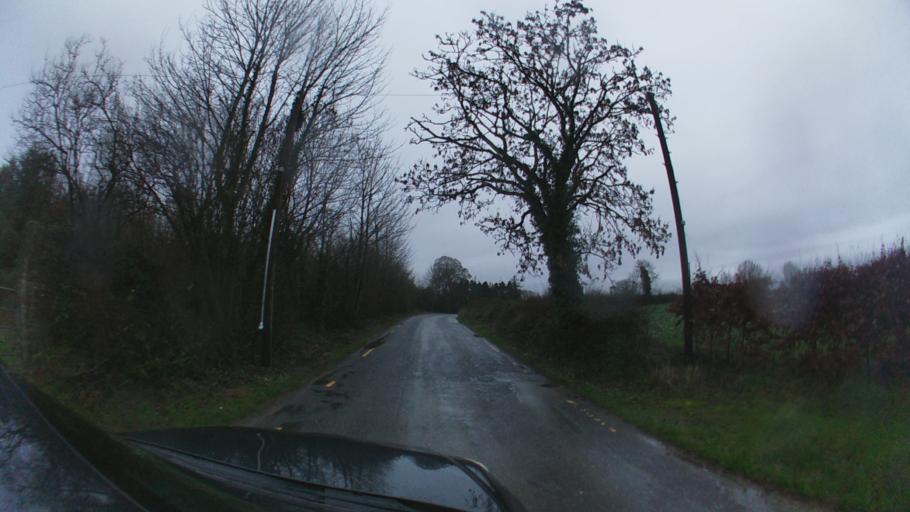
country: IE
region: Leinster
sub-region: County Carlow
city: Bagenalstown
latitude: 52.6206
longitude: -6.9911
